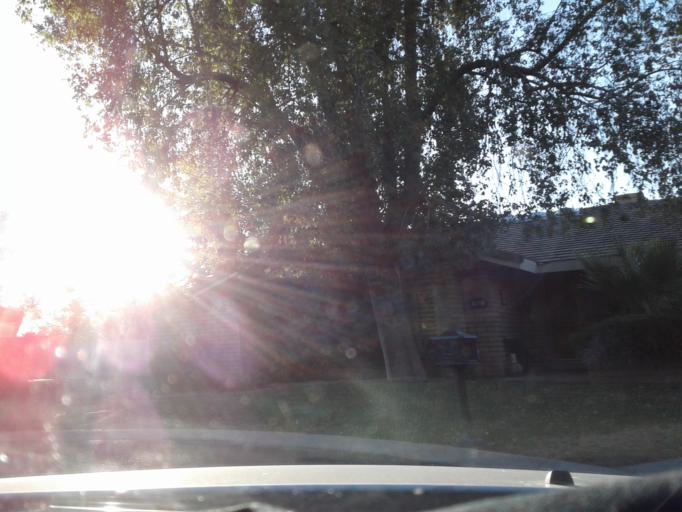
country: US
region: Arizona
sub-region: Maricopa County
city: Paradise Valley
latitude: 33.5230
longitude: -111.9843
